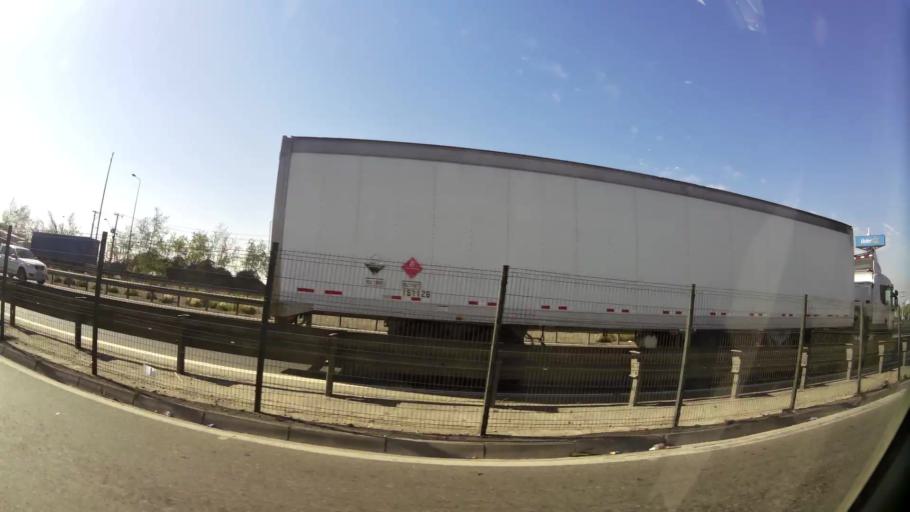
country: CL
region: Santiago Metropolitan
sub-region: Provincia de Santiago
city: Lo Prado
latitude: -33.5167
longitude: -70.7129
